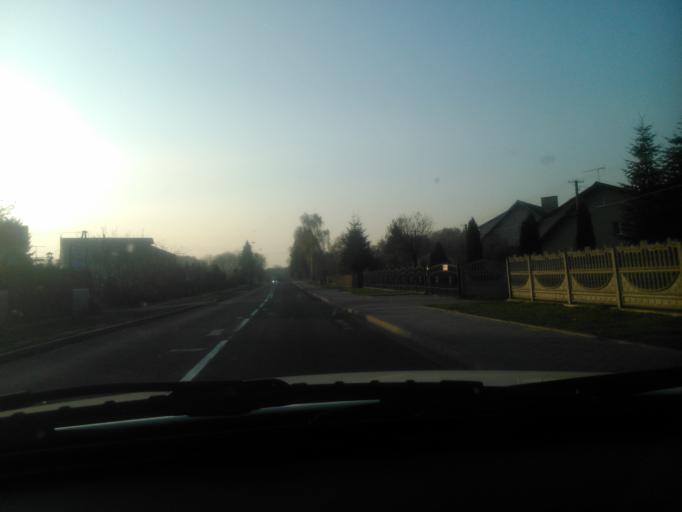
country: PL
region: Masovian Voivodeship
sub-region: Powiat mlawski
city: Szydlowo
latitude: 53.0798
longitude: 20.4578
